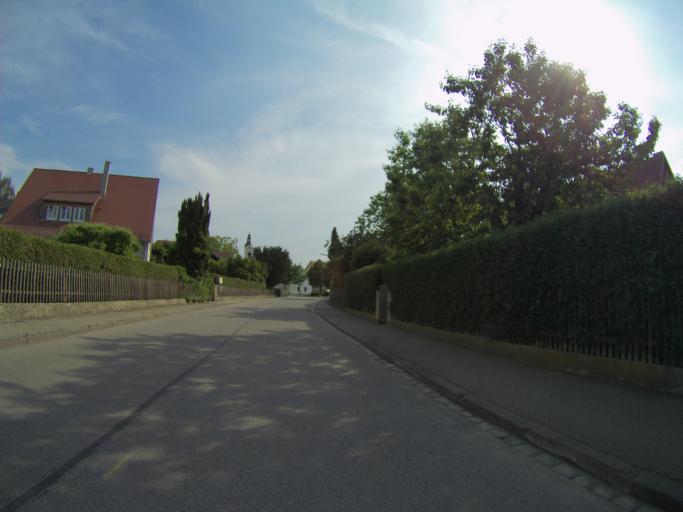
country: DE
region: Bavaria
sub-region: Upper Bavaria
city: Zolling
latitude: 48.4523
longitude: 11.7718
